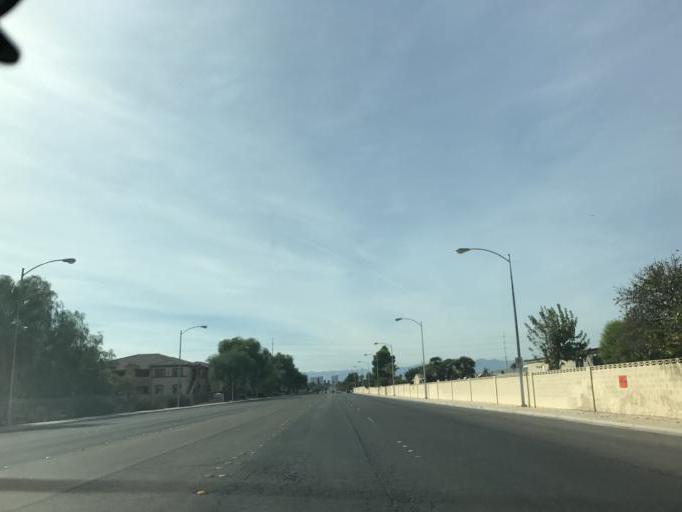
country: US
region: Nevada
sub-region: Clark County
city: Winchester
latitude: 36.1297
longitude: -115.0523
